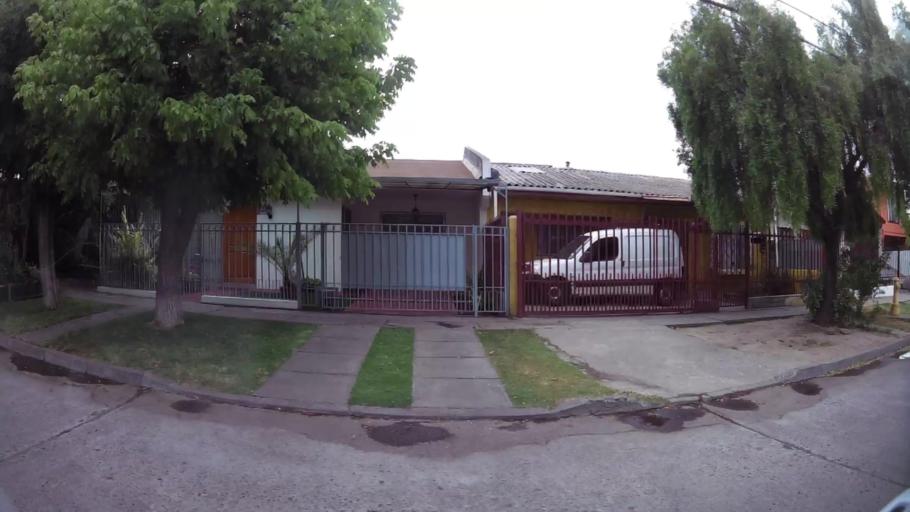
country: CL
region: O'Higgins
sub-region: Provincia de Cachapoal
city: Rancagua
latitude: -34.1529
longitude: -70.7345
